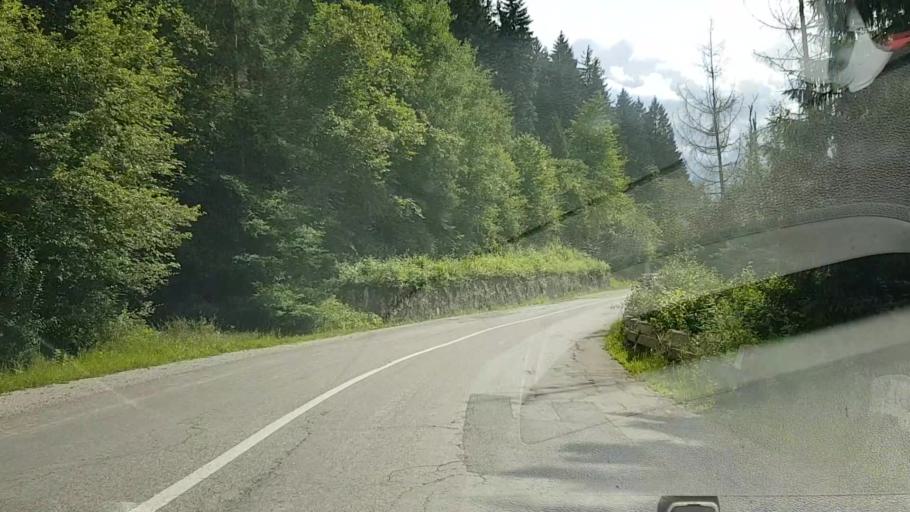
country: RO
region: Neamt
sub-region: Comuna Hangu
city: Hangu
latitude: 47.0171
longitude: 26.0870
